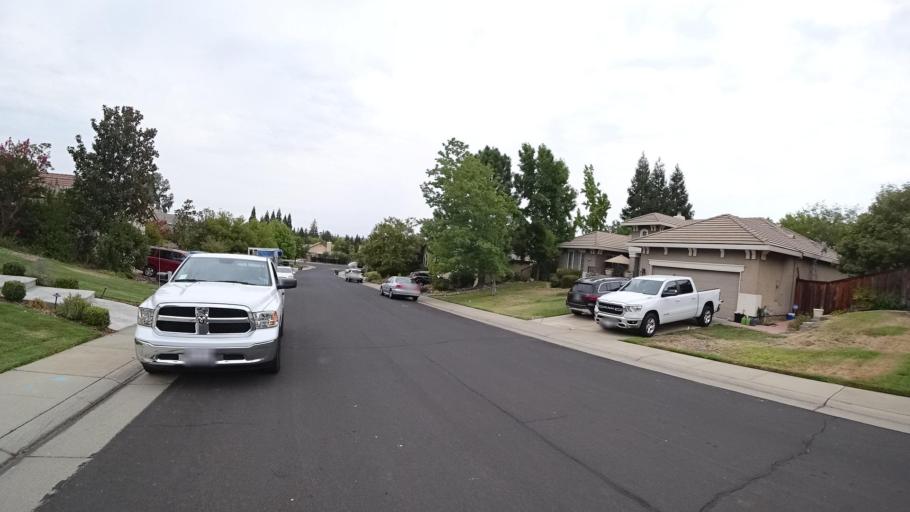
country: US
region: California
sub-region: Placer County
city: Rocklin
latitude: 38.7798
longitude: -121.2145
